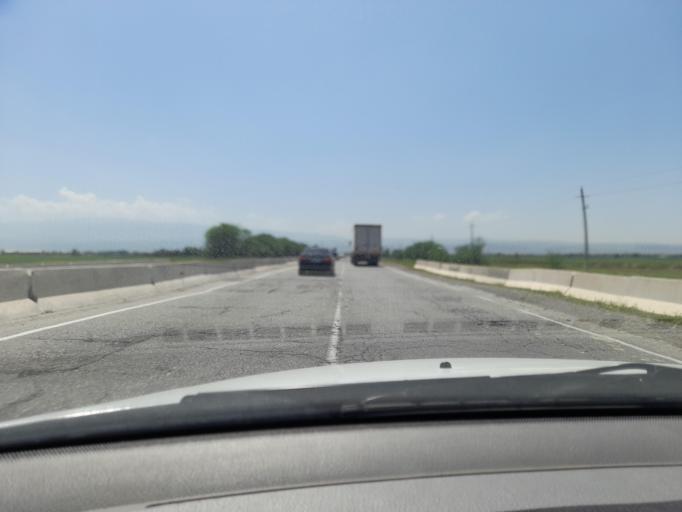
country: UZ
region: Jizzax
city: Jizzax
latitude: 40.1151
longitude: 67.9454
